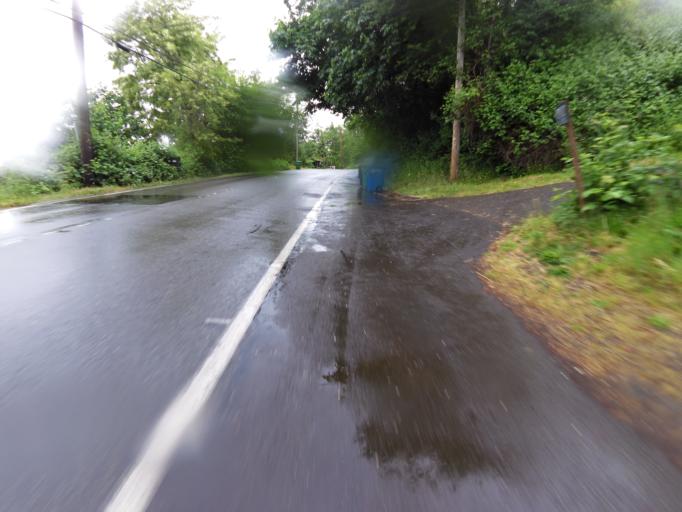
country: US
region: Washington
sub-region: King County
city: Bryn Mawr-Skyway
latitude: 47.5300
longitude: -122.2342
